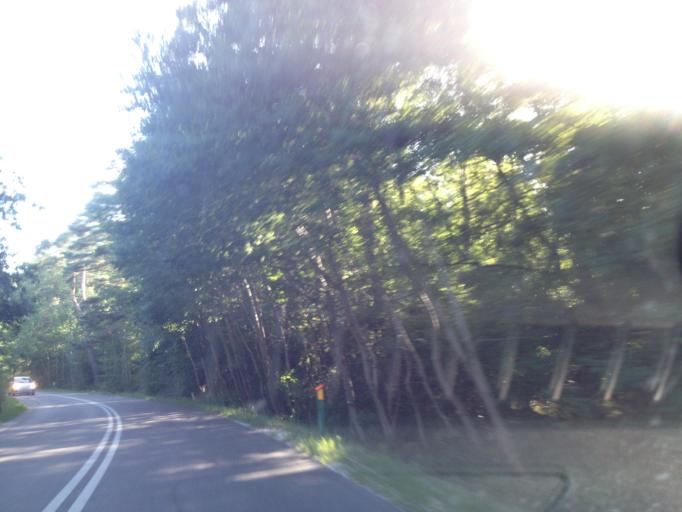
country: DK
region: Capital Region
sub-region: Halsnaes Kommune
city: Frederiksvaerk
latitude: 56.0276
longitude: 12.0824
